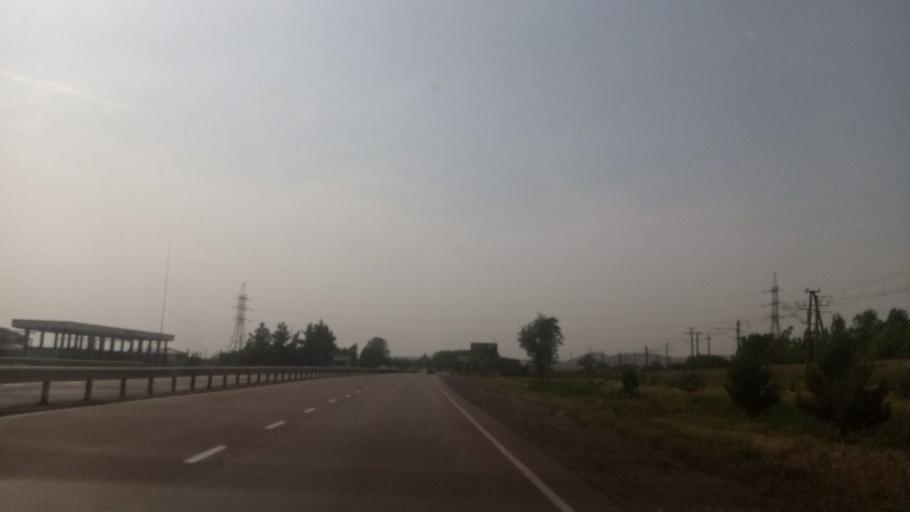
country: UZ
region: Toshkent
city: Ohangaron
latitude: 40.9079
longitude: 69.7951
